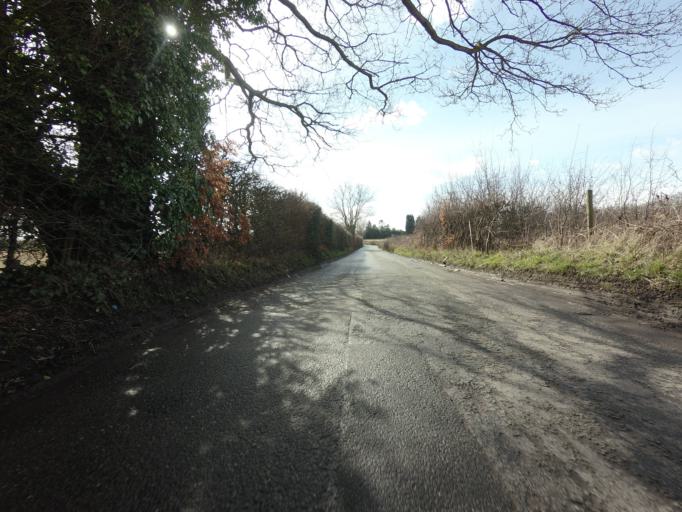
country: GB
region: England
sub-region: Kent
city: Swanley
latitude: 51.3899
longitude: 0.1345
